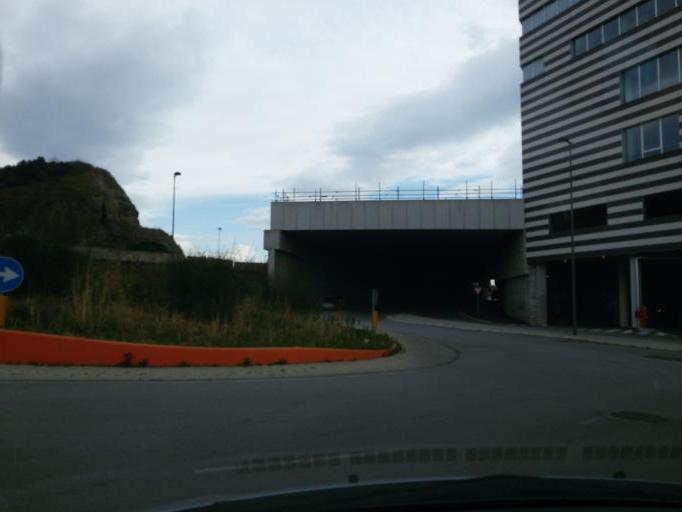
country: IT
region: Liguria
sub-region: Provincia di Genova
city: San Teodoro
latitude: 44.4265
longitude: 8.8628
